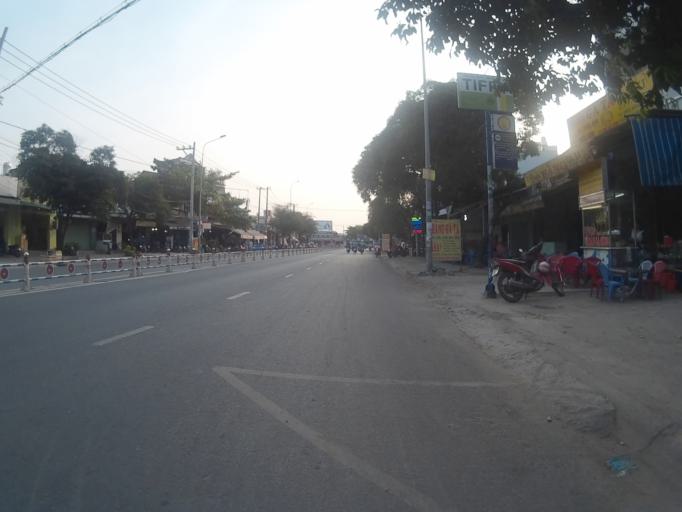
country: VN
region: Ho Chi Minh City
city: Ho Chi Minh City
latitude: 10.8096
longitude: 106.6194
